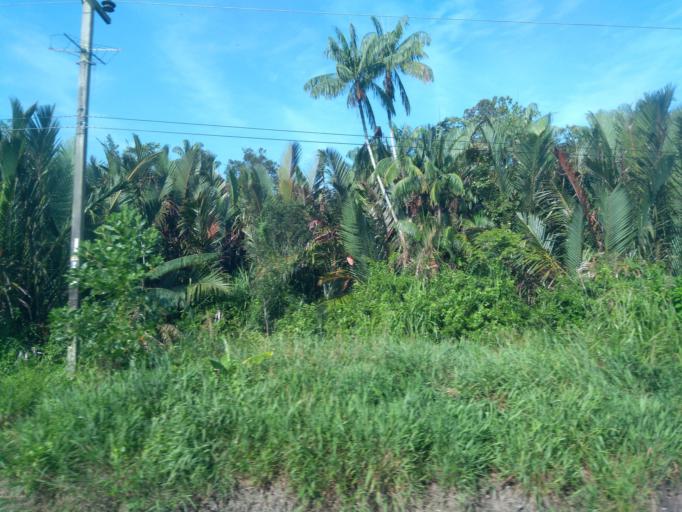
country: MY
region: Sarawak
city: Kuching
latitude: 1.6548
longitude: 110.4424
